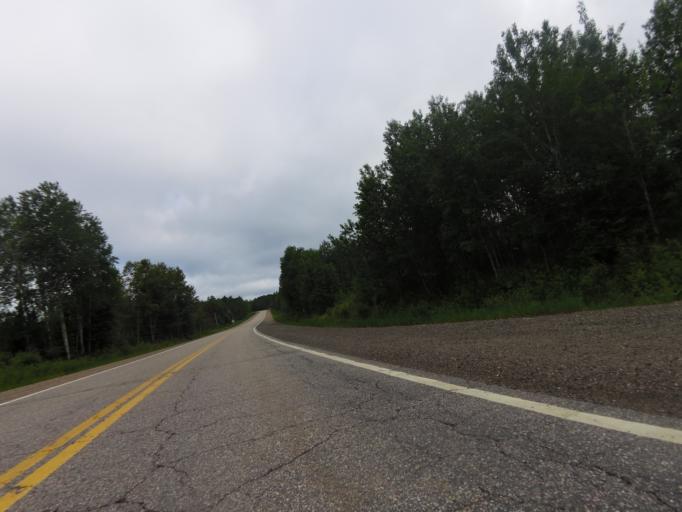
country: CA
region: Quebec
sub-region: Outaouais
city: Shawville
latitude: 45.9082
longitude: -76.3102
